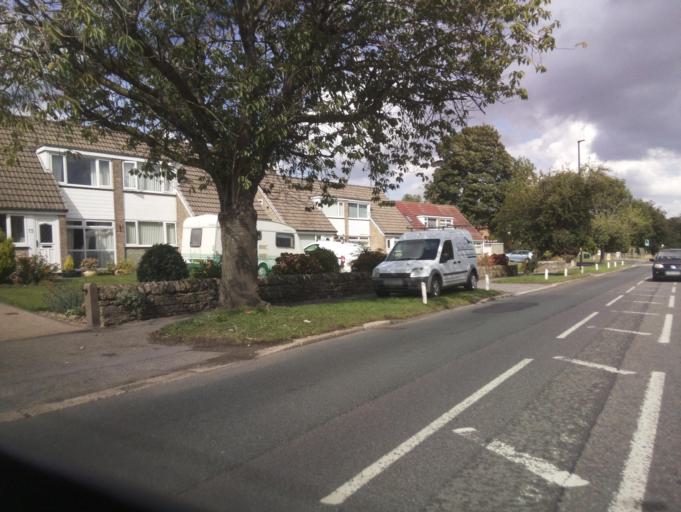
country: GB
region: England
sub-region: North Yorkshire
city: Catterick Garrison
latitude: 54.4095
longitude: -1.7208
